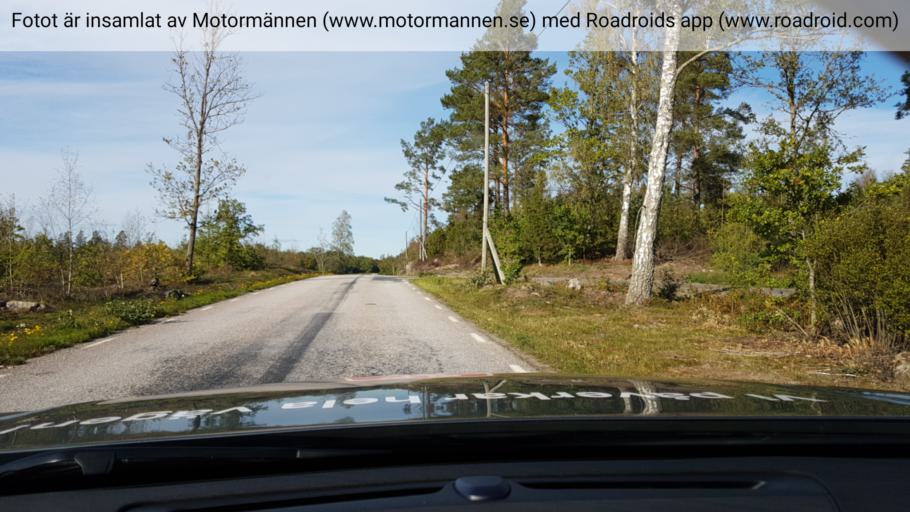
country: SE
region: OEstergoetland
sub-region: Valdemarsviks Kommun
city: Valdemarsvik
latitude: 58.0944
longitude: 16.6402
